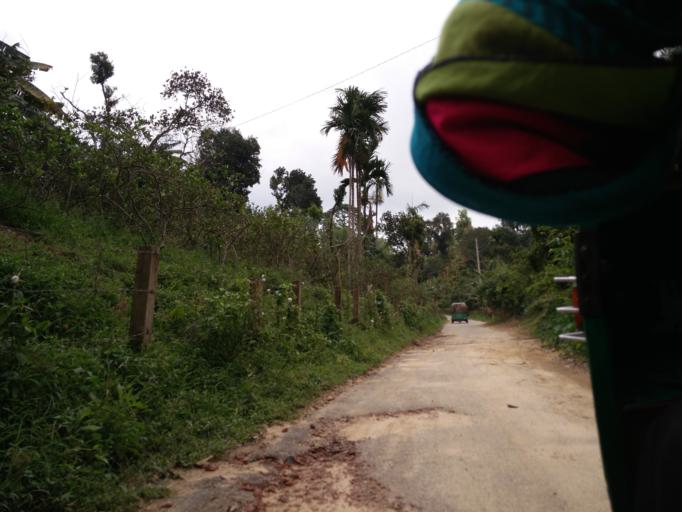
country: IN
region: Tripura
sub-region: Dhalai
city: Kamalpur
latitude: 24.3022
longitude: 91.7820
